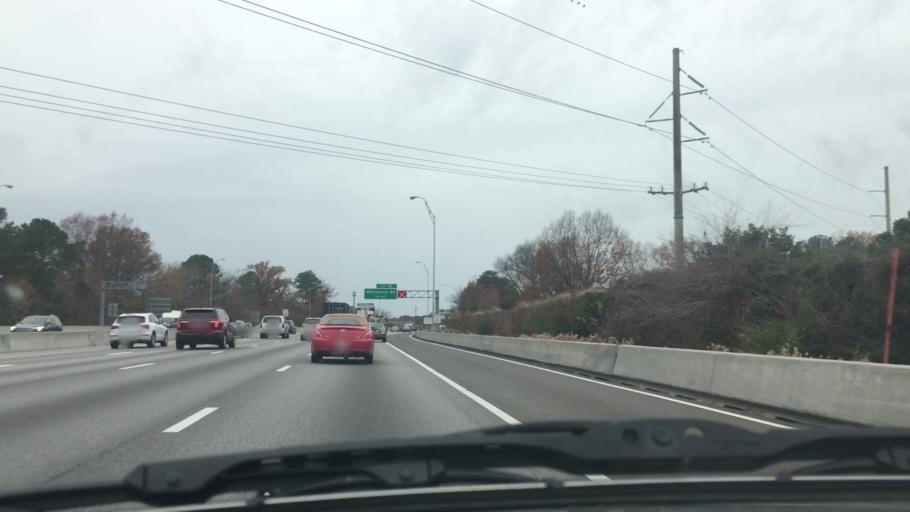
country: US
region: Virginia
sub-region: City of Chesapeake
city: Chesapeake
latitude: 36.8352
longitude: -76.1499
